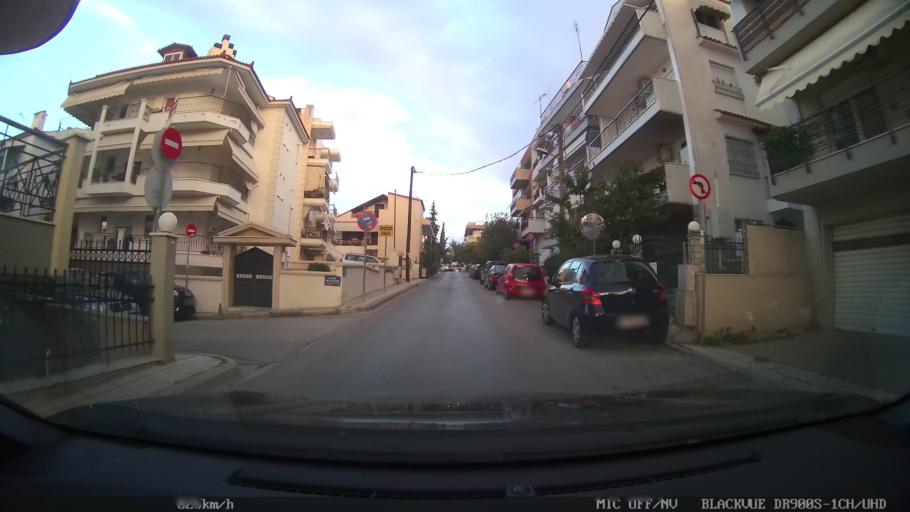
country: GR
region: Central Macedonia
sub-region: Nomos Thessalonikis
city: Pylaia
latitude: 40.5991
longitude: 22.9898
